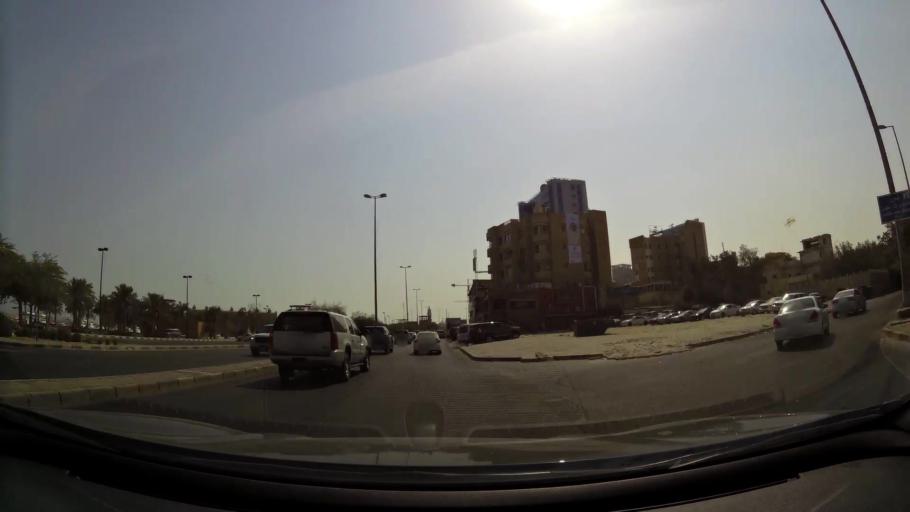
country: KW
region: Al Ahmadi
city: Al Fahahil
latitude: 29.0836
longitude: 48.1397
